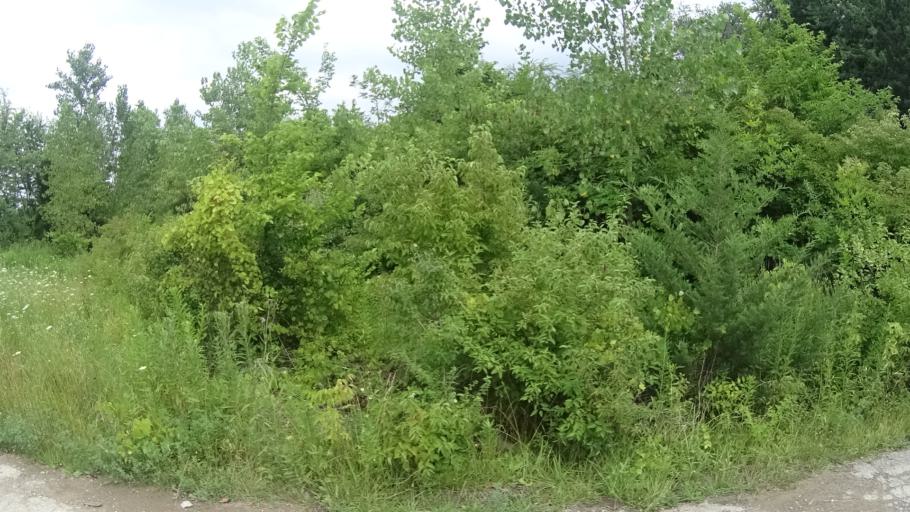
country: US
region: Ohio
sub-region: Erie County
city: Sandusky
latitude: 41.4441
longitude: -82.7407
